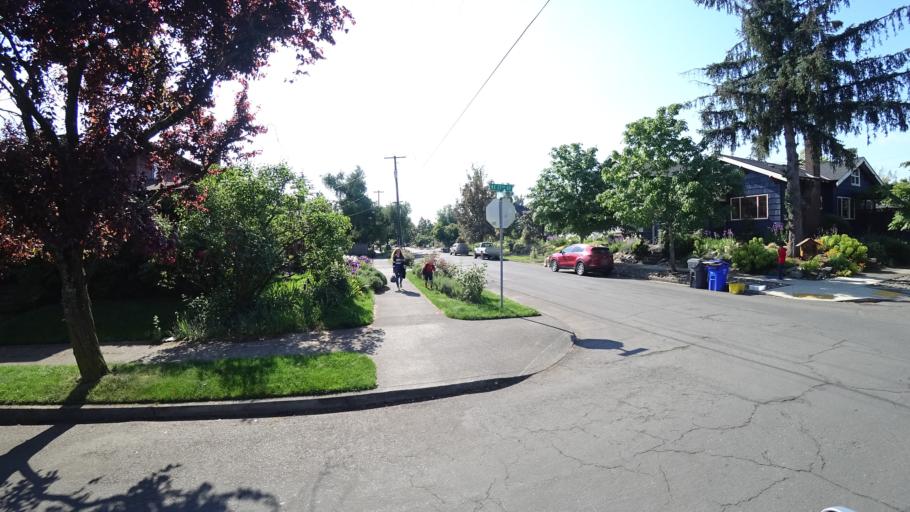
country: US
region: Oregon
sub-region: Multnomah County
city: Portland
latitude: 45.5530
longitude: -122.6419
